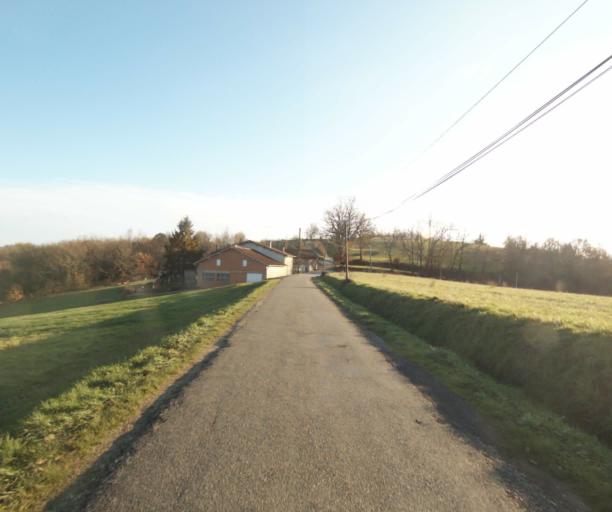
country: FR
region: Midi-Pyrenees
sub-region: Departement du Tarn-et-Garonne
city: Moissac
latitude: 44.1318
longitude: 1.1382
